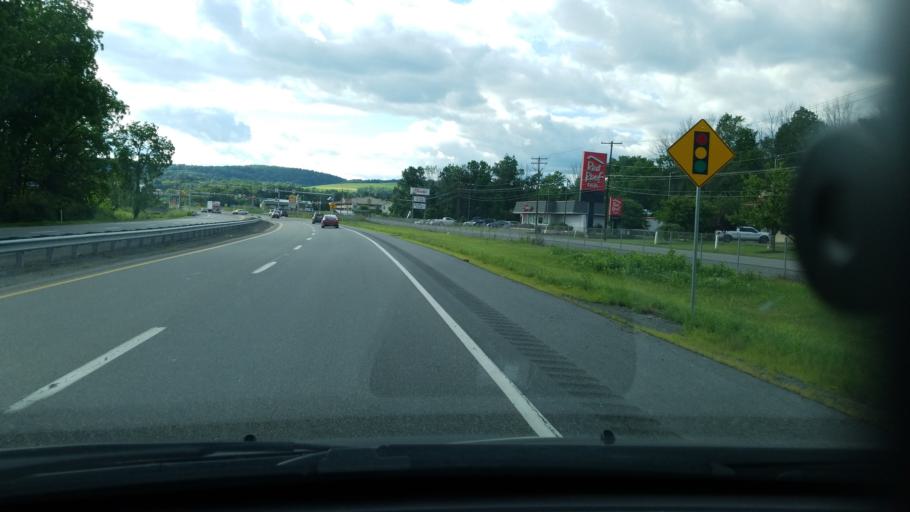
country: US
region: Pennsylvania
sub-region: Northumberland County
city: Riverside
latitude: 40.9933
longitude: -76.6381
